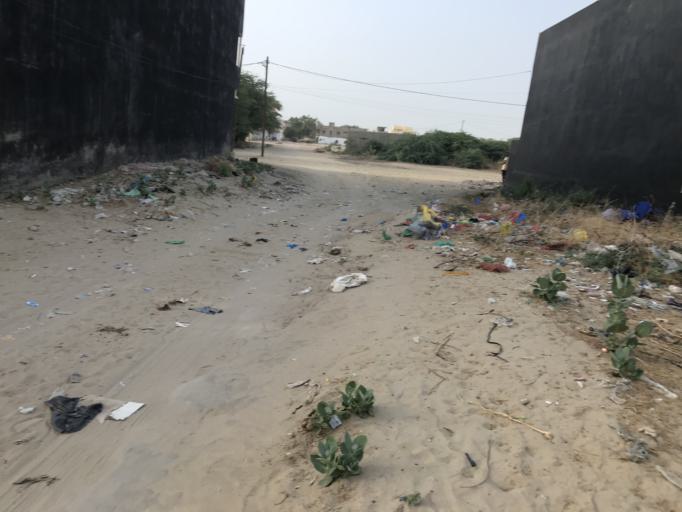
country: SN
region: Saint-Louis
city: Saint-Louis
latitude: 16.0369
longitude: -16.4458
